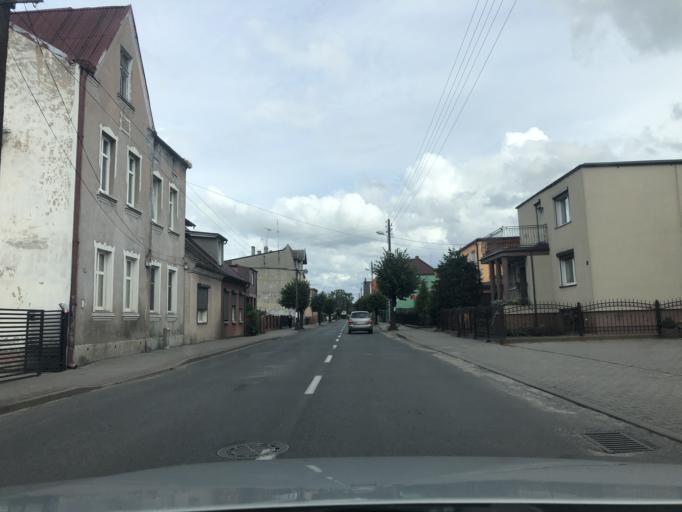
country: PL
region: Greater Poland Voivodeship
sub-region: Powiat czarnkowsko-trzcianecki
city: Krzyz Wielkopolski
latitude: 52.8811
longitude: 16.0154
